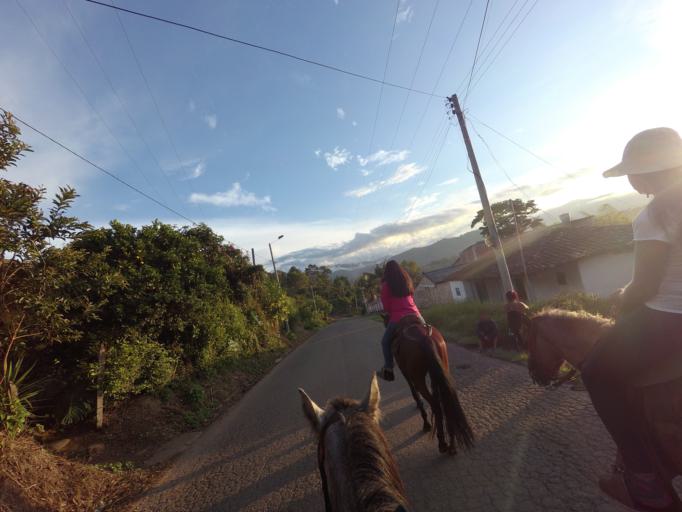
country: CO
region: Huila
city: San Agustin
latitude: 1.8899
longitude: -76.2715
